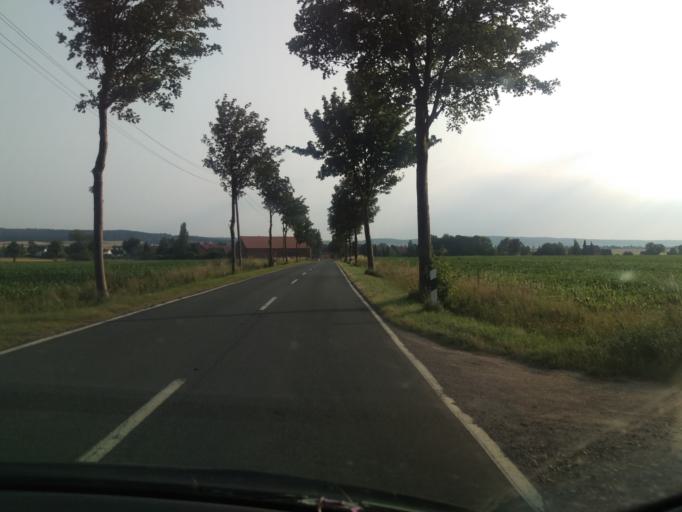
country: DE
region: Lower Saxony
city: Schellerten
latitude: 52.1729
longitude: 10.0965
